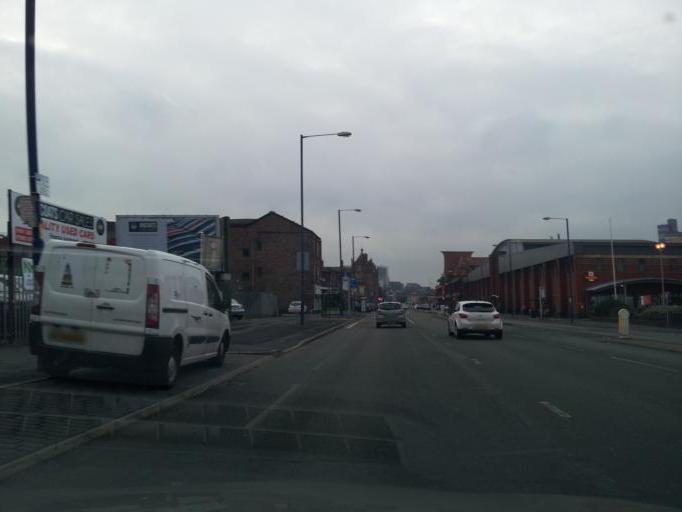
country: GB
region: England
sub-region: Manchester
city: Manchester
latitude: 53.4877
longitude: -2.2252
